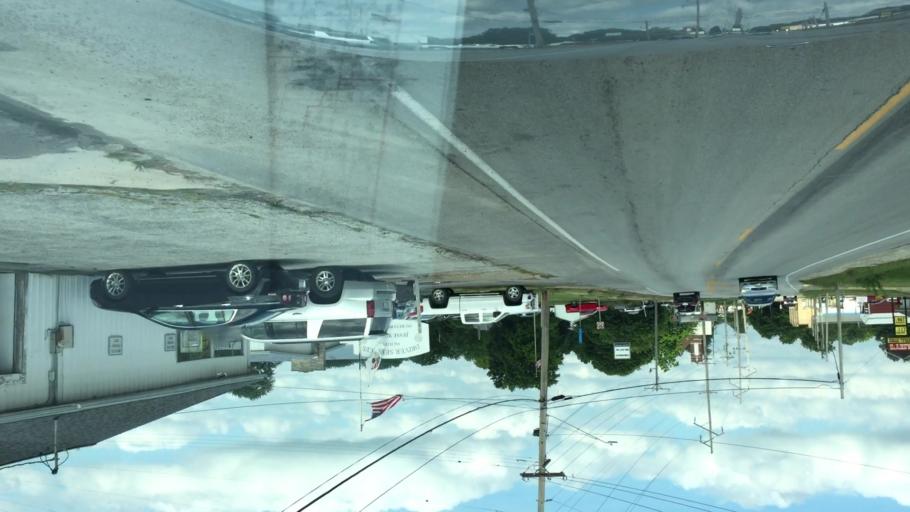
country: US
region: Illinois
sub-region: Hancock County
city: Carthage
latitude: 40.4162
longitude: -91.1434
